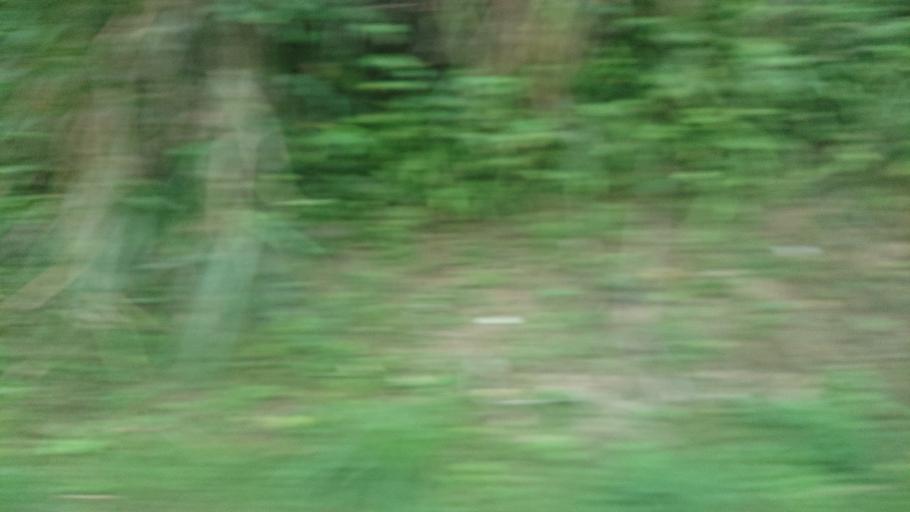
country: TW
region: Taiwan
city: Daxi
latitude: 24.8905
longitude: 121.3769
